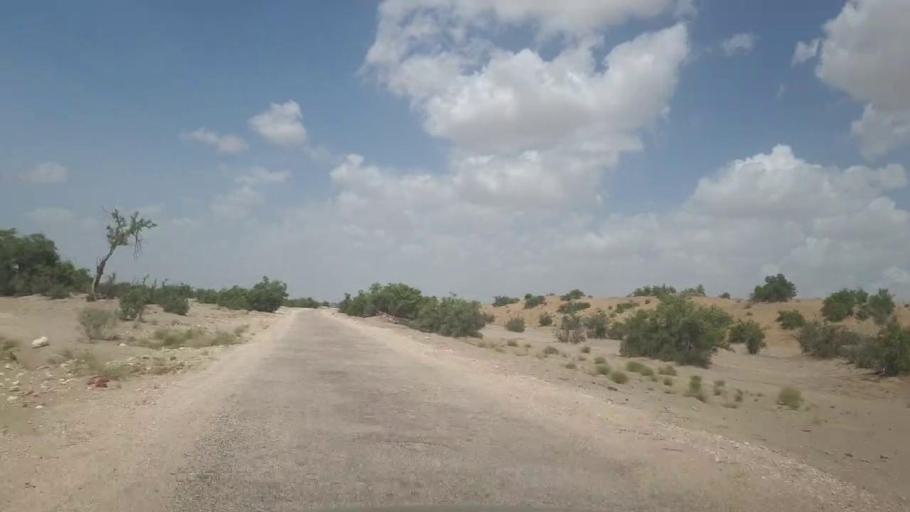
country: PK
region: Sindh
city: Kot Diji
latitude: 27.2537
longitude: 69.1646
